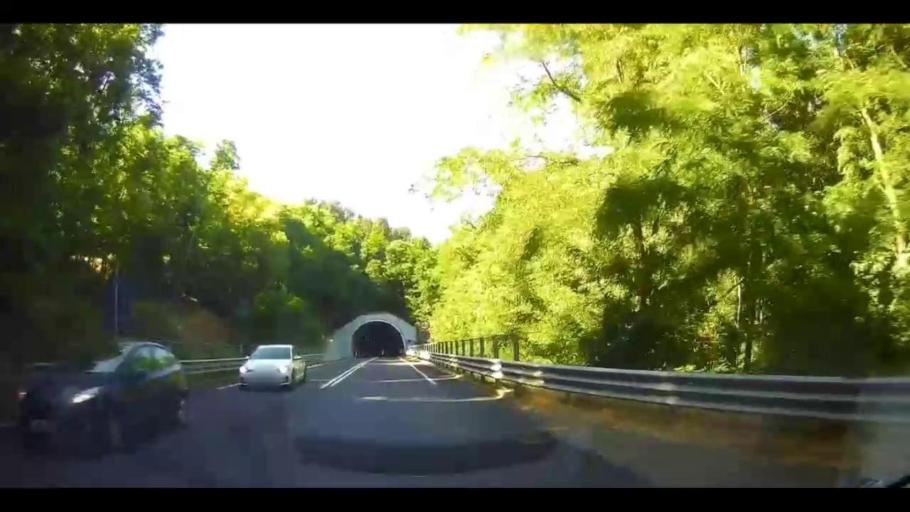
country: IT
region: Calabria
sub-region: Provincia di Cosenza
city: Spezzano della Sila
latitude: 39.3003
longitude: 16.3559
